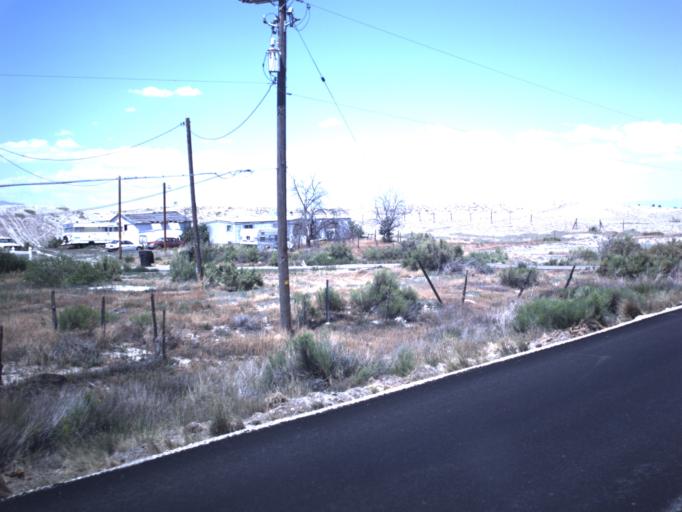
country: US
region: Utah
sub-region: Emery County
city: Castle Dale
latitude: 39.2366
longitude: -111.0065
